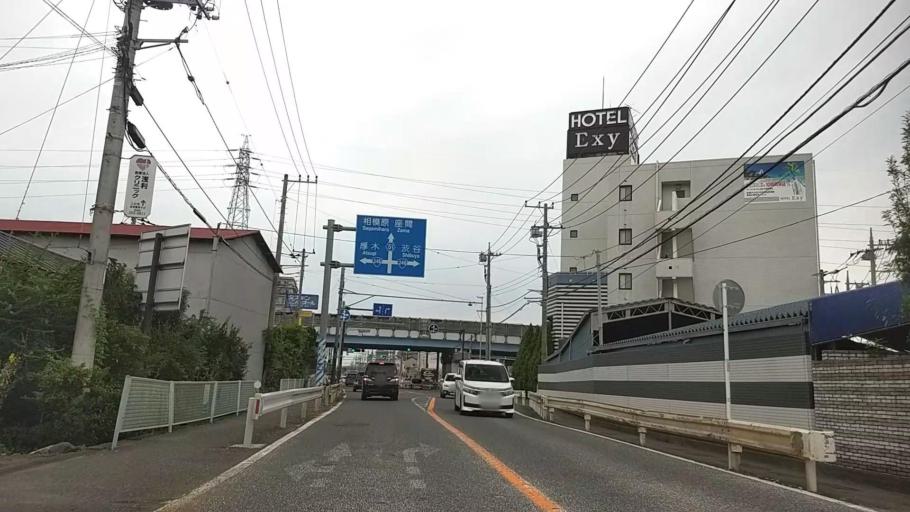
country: JP
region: Kanagawa
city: Zama
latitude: 35.4632
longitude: 139.3884
